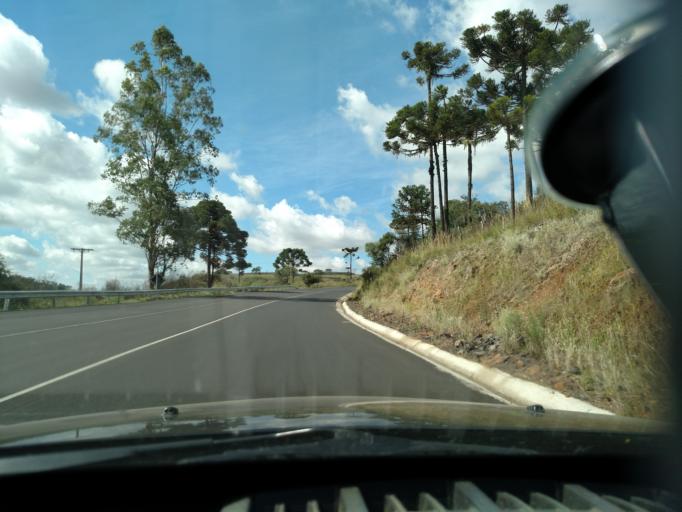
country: BR
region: Santa Catarina
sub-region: Sao Joaquim
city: Sao Joaquim
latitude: -28.1000
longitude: -50.0512
